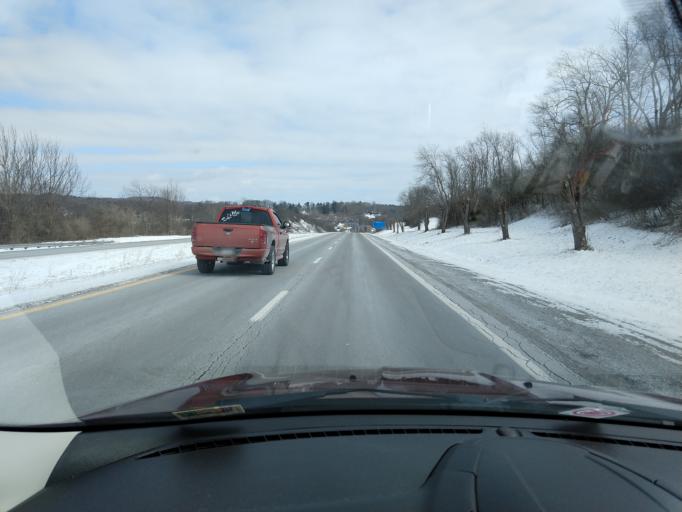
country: US
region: West Virginia
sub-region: Mercer County
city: Bluefield
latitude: 37.2417
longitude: -81.2386
